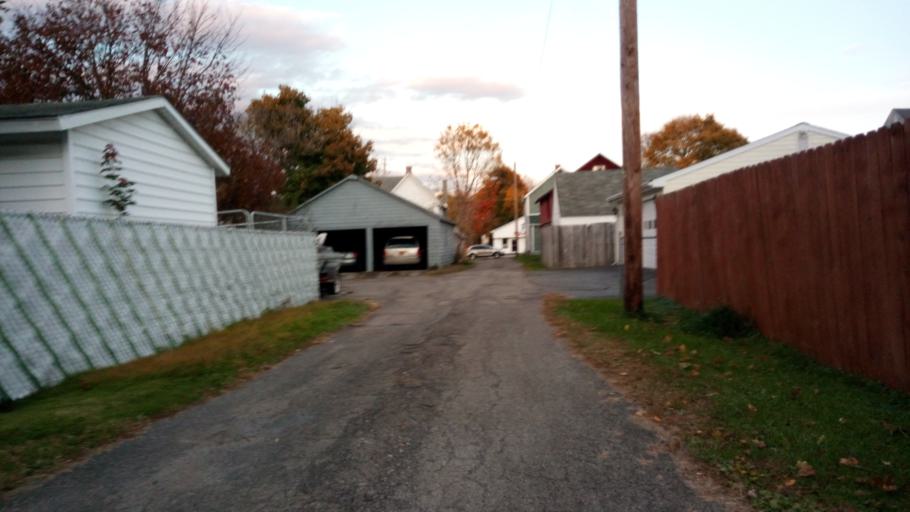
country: US
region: New York
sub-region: Chemung County
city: Elmira
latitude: 42.0768
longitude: -76.8137
